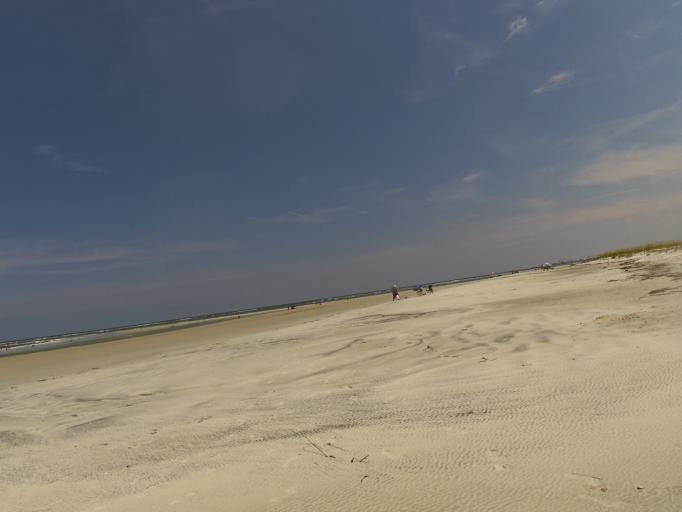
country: US
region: Florida
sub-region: Duval County
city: Atlantic Beach
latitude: 30.4362
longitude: -81.4074
